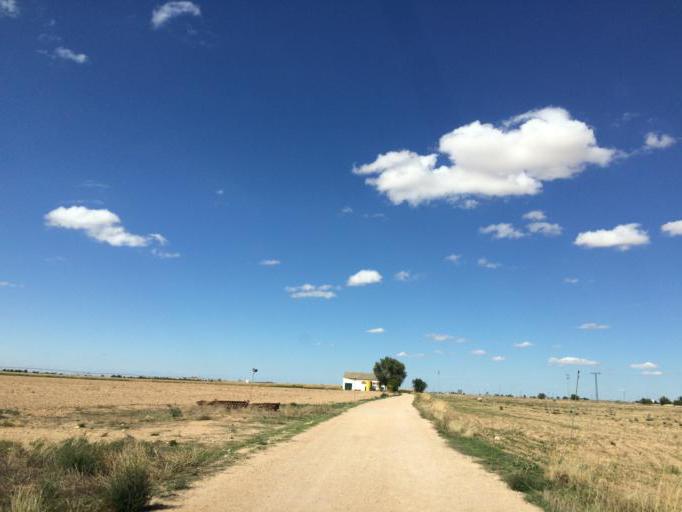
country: ES
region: Castille-La Mancha
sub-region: Provincia de Albacete
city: Albacete
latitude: 38.9381
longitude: -1.8388
